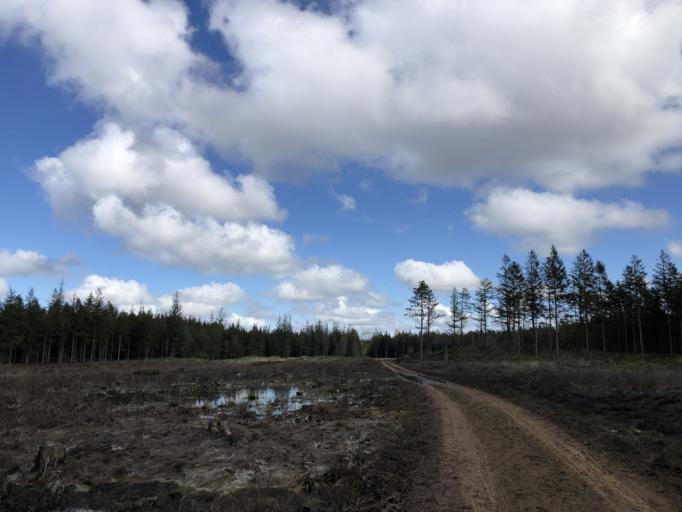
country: DK
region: Central Jutland
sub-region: Holstebro Kommune
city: Ulfborg
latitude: 56.2448
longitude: 8.4686
